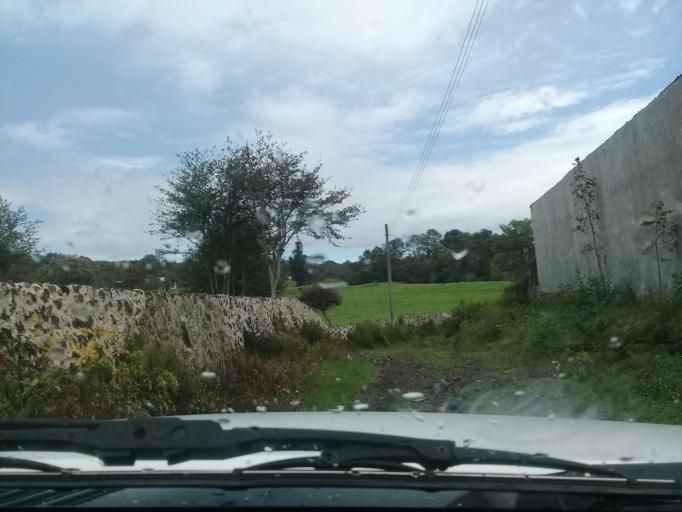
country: MX
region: Veracruz
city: Rafael Lucio
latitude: 19.6165
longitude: -96.9985
